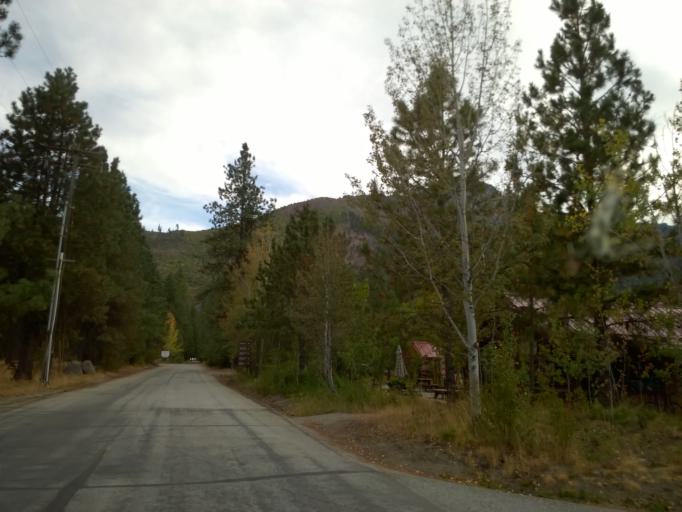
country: US
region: Washington
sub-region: Chelan County
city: Leavenworth
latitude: 47.5533
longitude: -120.6802
